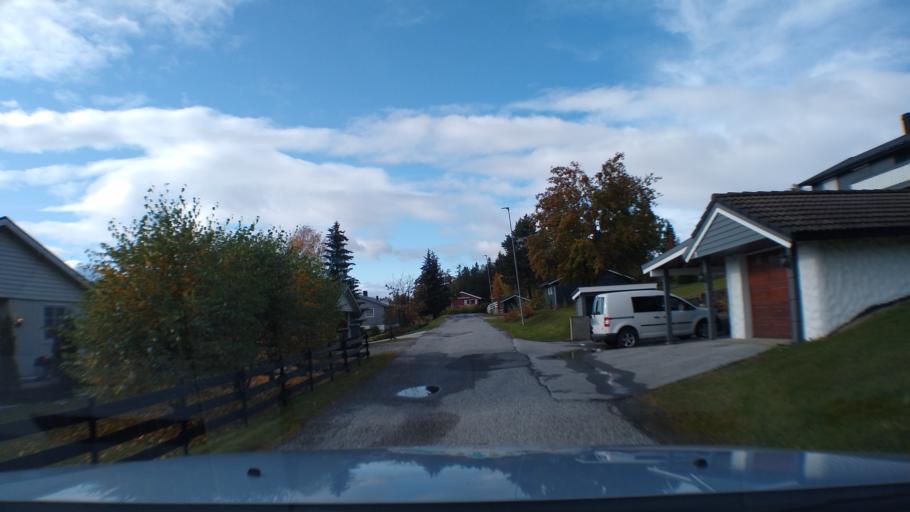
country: NO
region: Oppland
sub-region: Ringebu
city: Ringebu
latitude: 61.5415
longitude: 10.1234
